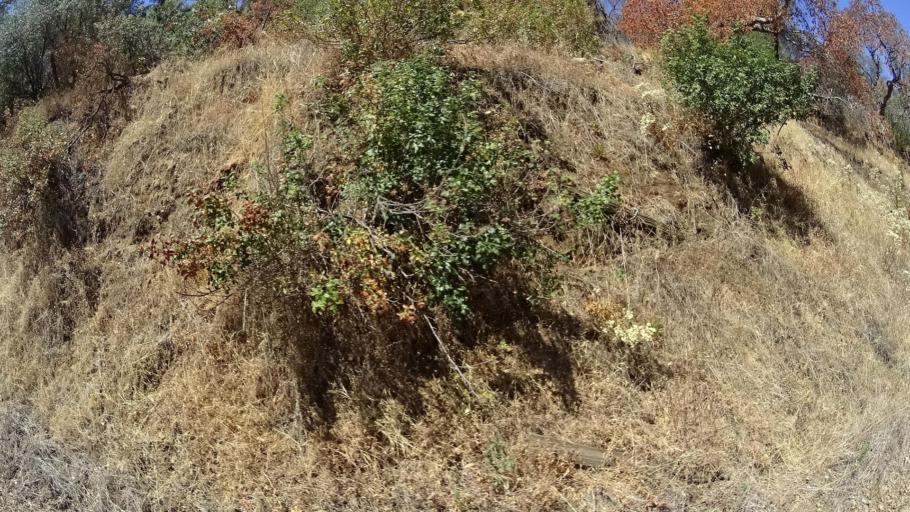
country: US
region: California
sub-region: Mariposa County
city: Mariposa
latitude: 37.3788
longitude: -119.9656
